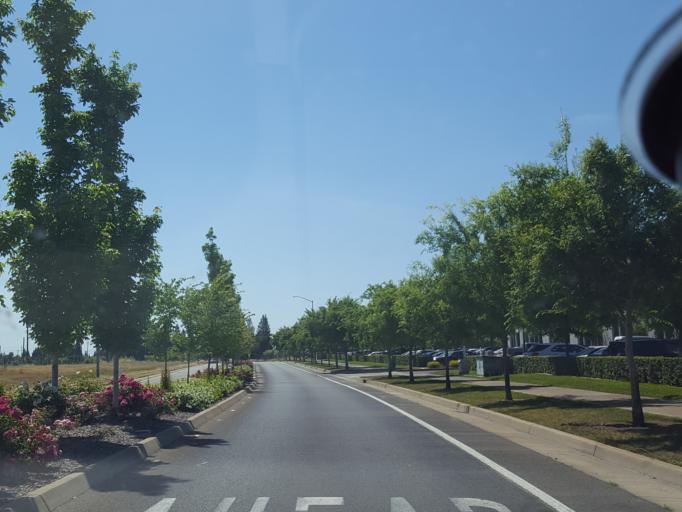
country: US
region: California
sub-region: Sacramento County
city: Rancho Cordova
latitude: 38.5667
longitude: -121.3030
